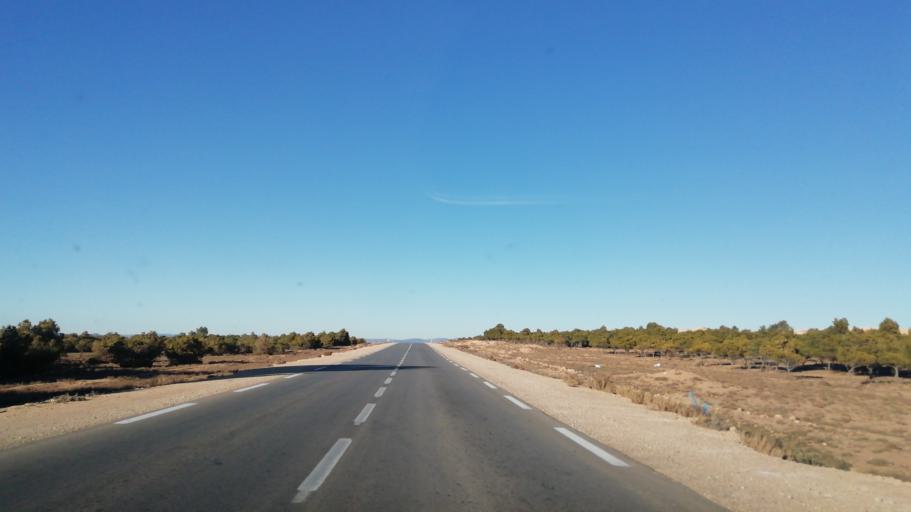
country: DZ
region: Tlemcen
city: Sebdou
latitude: 34.4423
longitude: -1.2760
